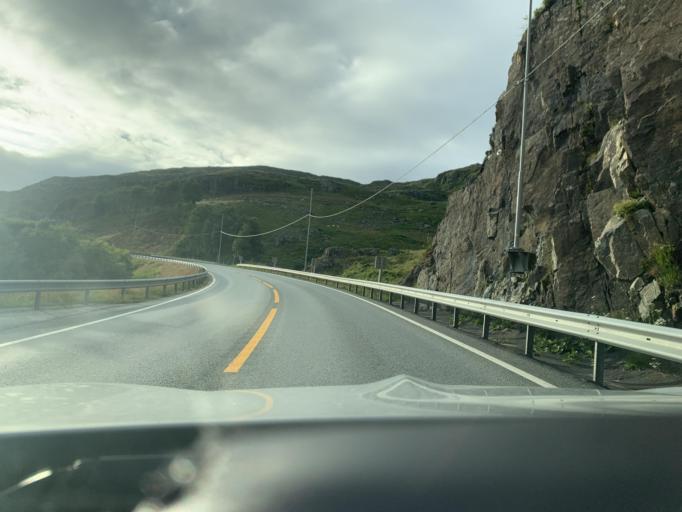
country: NO
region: Rogaland
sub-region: Bjerkreim
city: Vikesa
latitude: 58.6607
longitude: 6.0182
